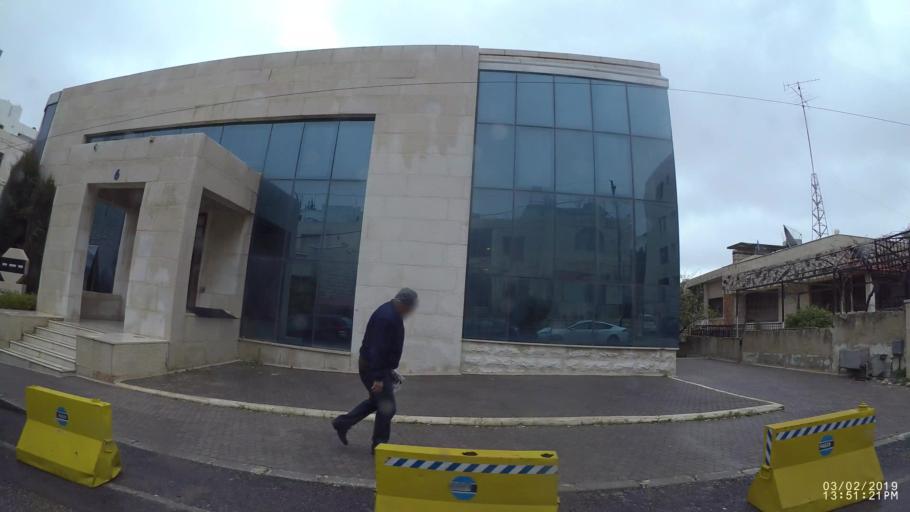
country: JO
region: Amman
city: Amman
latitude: 31.9614
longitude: 35.9008
